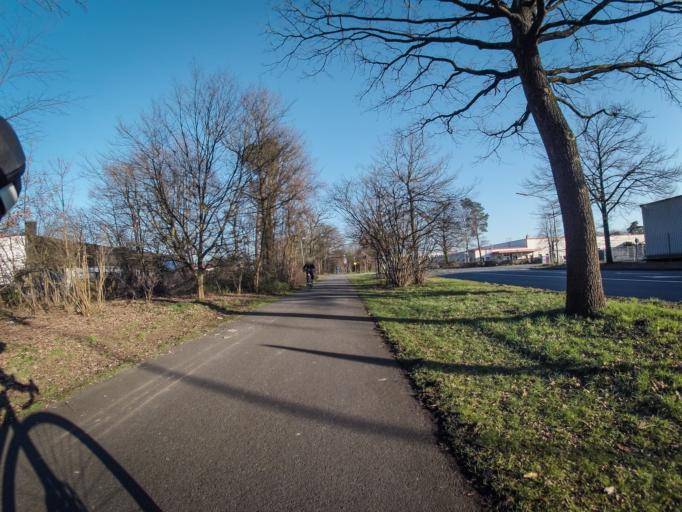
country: DE
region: Lower Saxony
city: Wallenhorst
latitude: 52.3050
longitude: 8.0037
